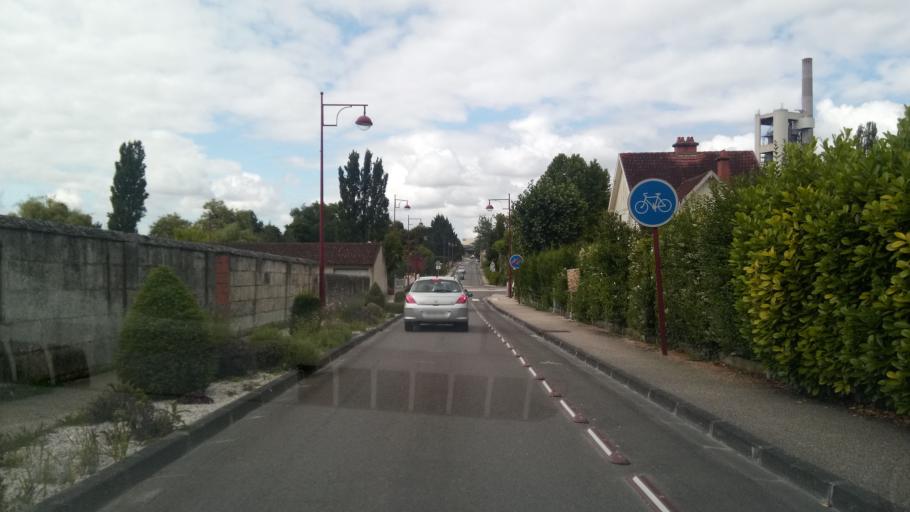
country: FR
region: Poitou-Charentes
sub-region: Departement de la Charente
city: La Couronne
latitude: 45.6105
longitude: 0.1013
